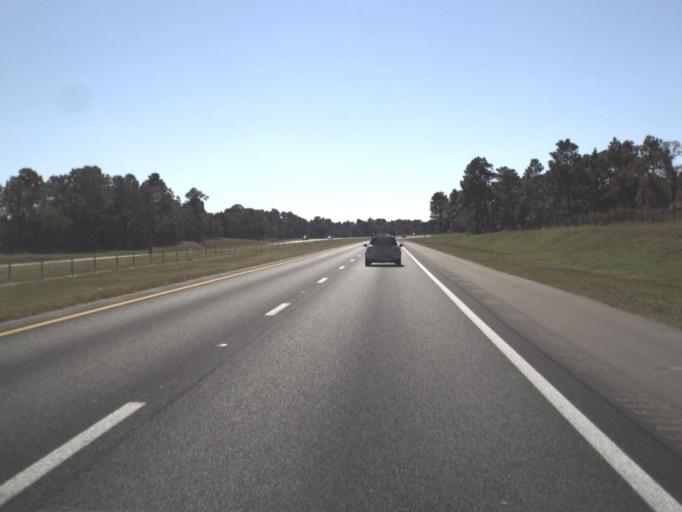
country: US
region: Florida
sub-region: Hernando County
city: Brookridge
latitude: 28.5049
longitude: -82.4770
